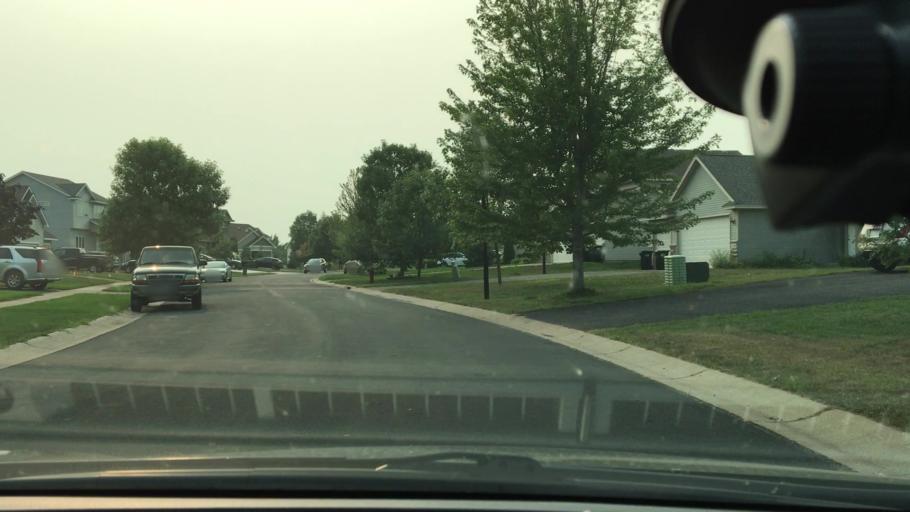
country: US
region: Minnesota
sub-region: Wright County
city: Albertville
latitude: 45.2549
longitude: -93.6554
